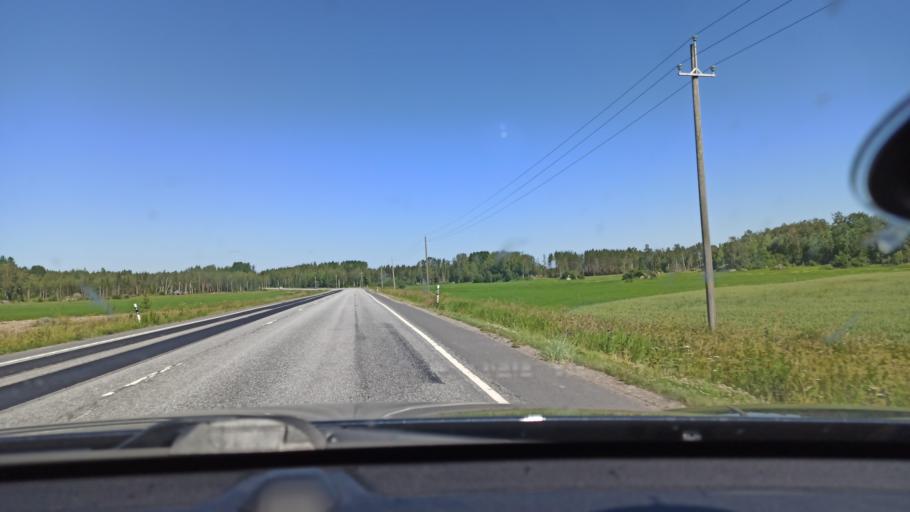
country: FI
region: Ostrobothnia
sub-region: Vaasa
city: Voera
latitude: 63.2188
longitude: 22.2183
